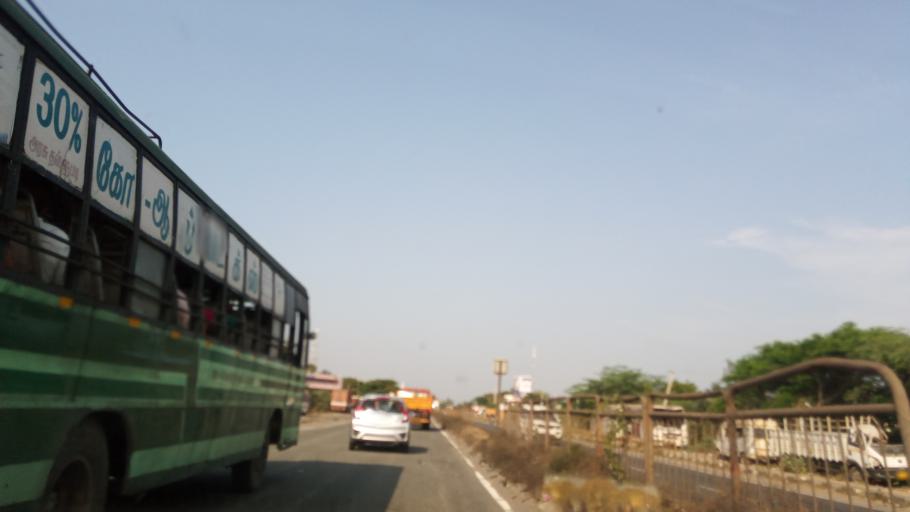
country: IN
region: Tamil Nadu
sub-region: Kancheepuram
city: Sriperumbudur
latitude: 12.9630
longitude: 79.9463
